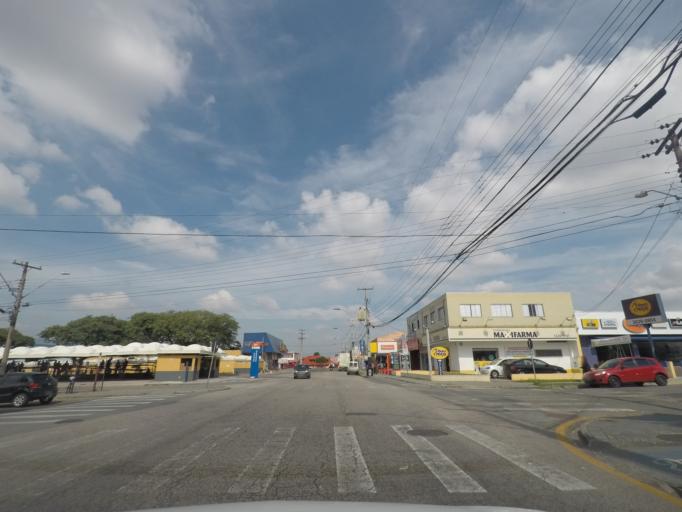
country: BR
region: Parana
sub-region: Pinhais
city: Pinhais
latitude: -25.4687
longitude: -49.2087
